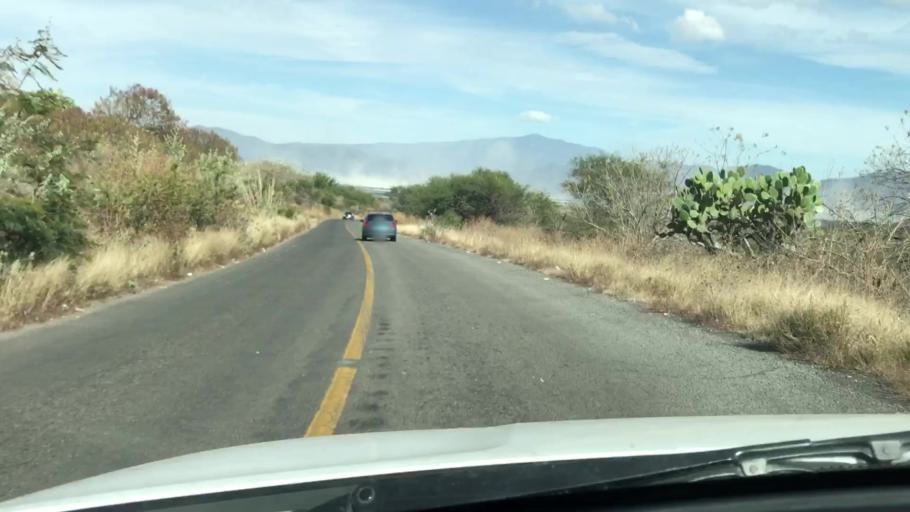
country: MX
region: Jalisco
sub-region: Zacoalco de Torres
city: Barranca de Otates (Barranca de Otatan)
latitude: 20.2595
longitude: -103.6527
